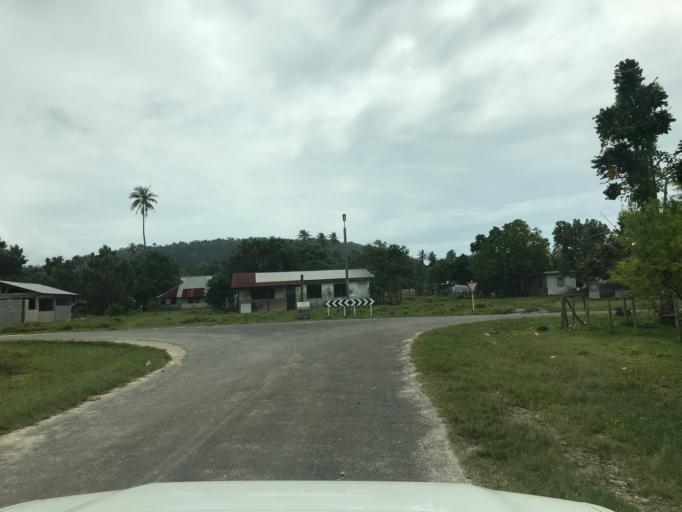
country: VU
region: Sanma
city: Port-Olry
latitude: -15.0425
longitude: 167.0721
